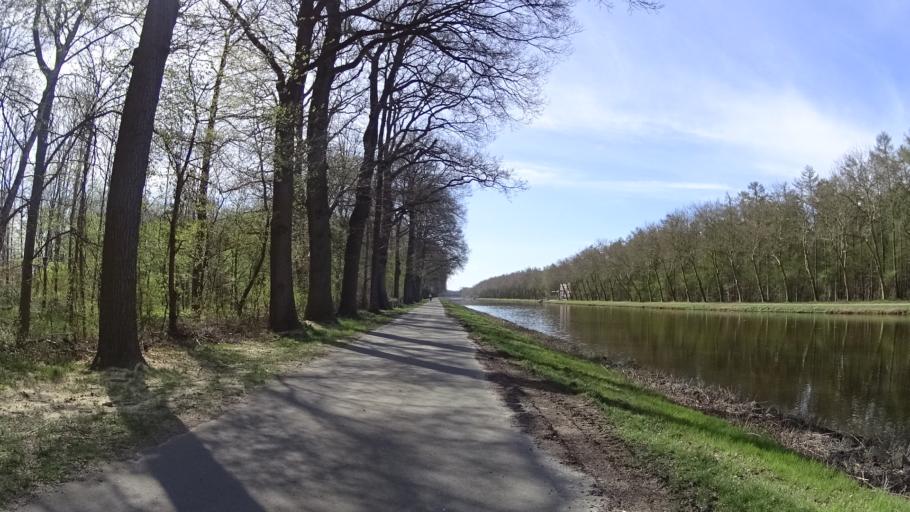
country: DE
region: Lower Saxony
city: Geeste
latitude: 52.5891
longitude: 7.3108
